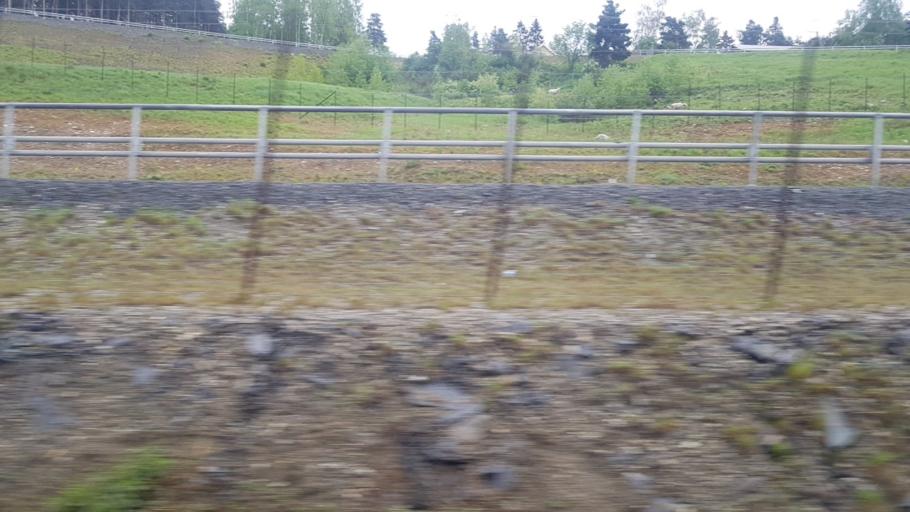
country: NO
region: Oppland
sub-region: Sor-Fron
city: Hundorp
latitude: 61.5619
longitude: 9.9217
